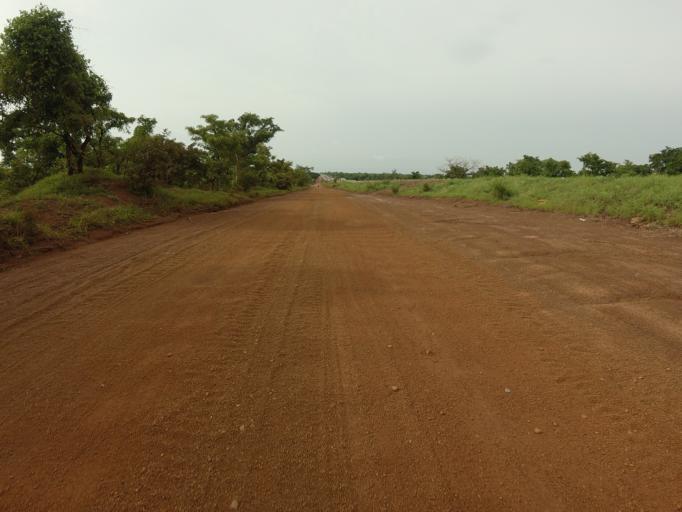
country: GH
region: Northern
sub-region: Yendi
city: Yendi
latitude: 9.6578
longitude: -0.0734
